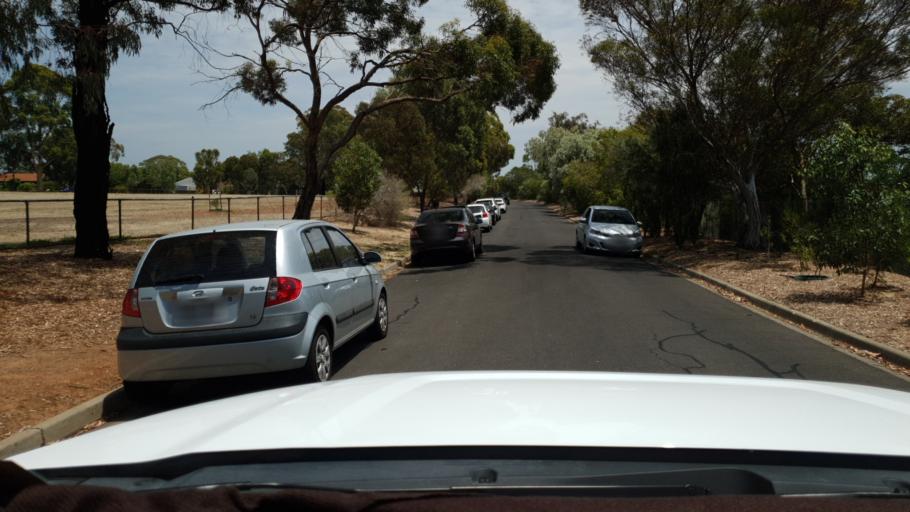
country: AU
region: South Australia
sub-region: Mitcham
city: Clapham
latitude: -35.0000
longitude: 138.5879
